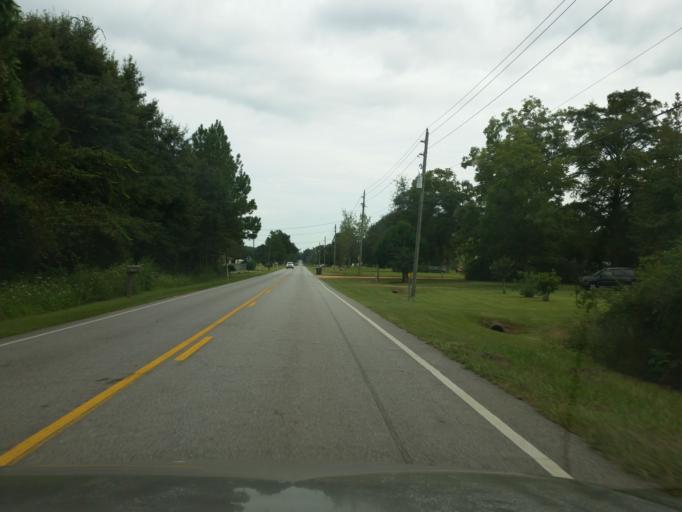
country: US
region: Florida
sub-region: Escambia County
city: Molino
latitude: 30.6954
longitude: -87.3317
